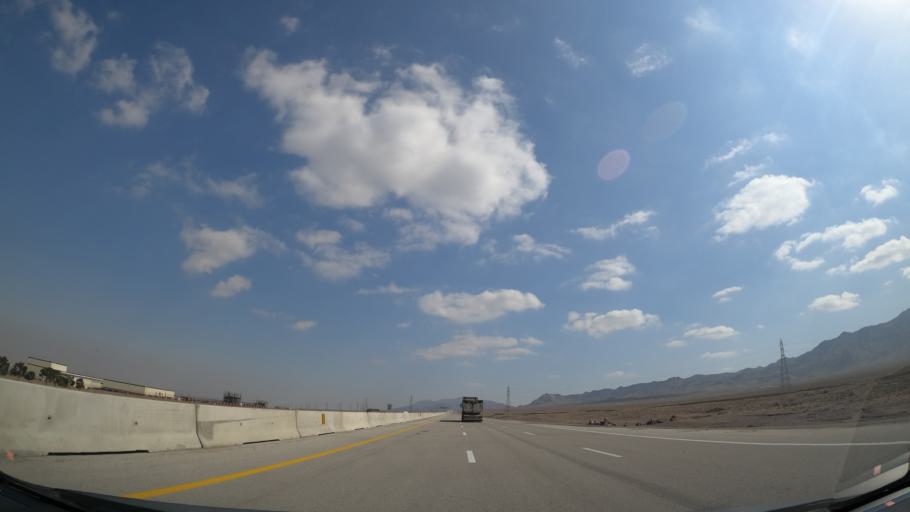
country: IR
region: Alborz
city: Eshtehard
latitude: 35.7175
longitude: 50.5751
